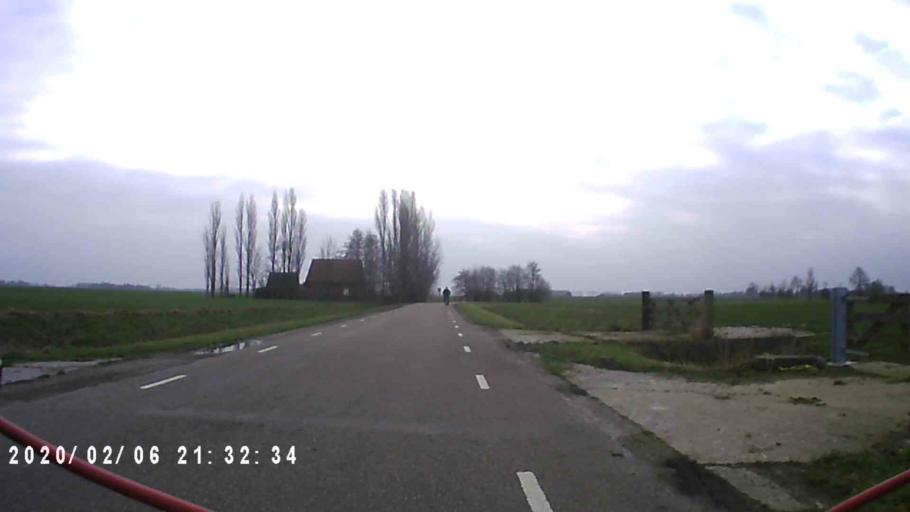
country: NL
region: Groningen
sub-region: Gemeente Zuidhorn
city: Noordhorn
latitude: 53.2794
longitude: 6.3895
